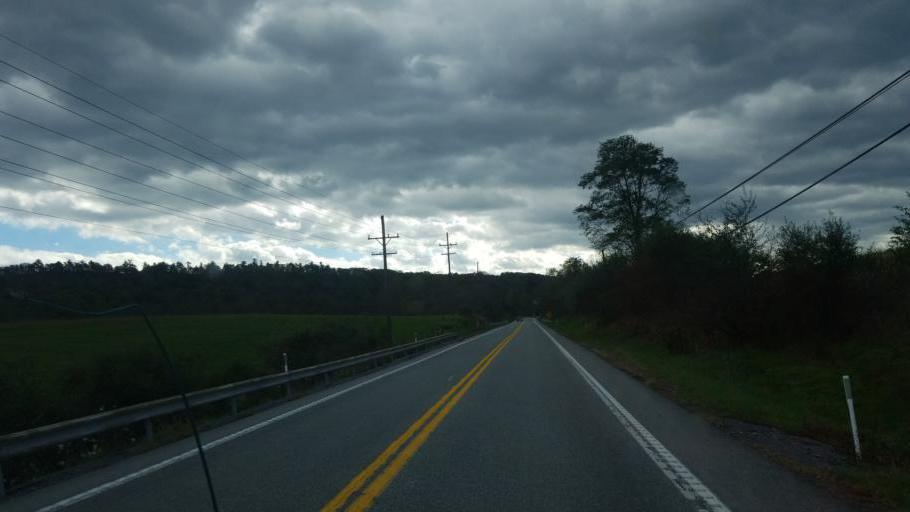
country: US
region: Pennsylvania
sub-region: Fulton County
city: McConnellsburg
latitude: 39.9515
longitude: -78.0233
